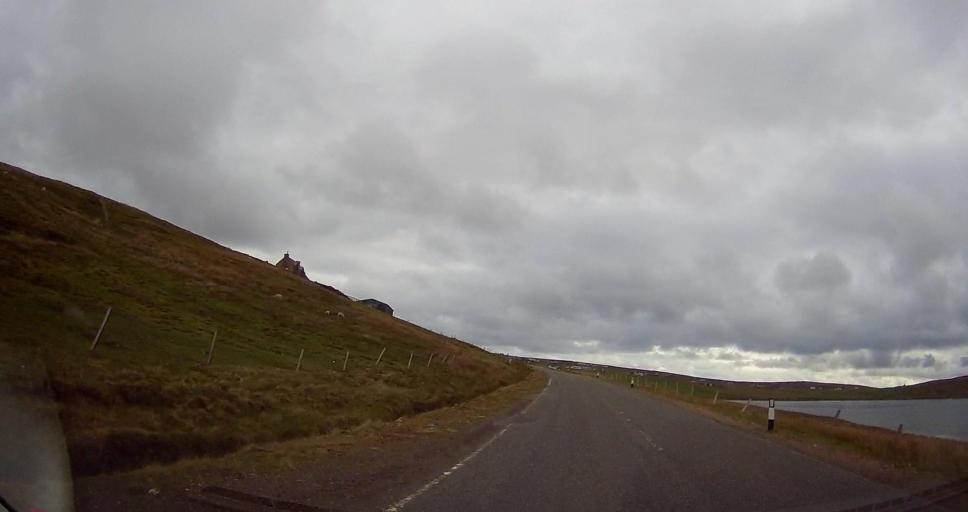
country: GB
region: Scotland
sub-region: Shetland Islands
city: Shetland
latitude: 60.6076
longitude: -1.0821
